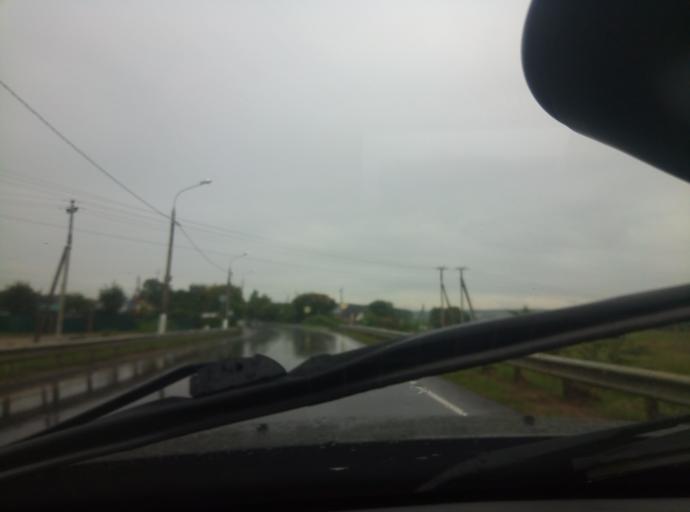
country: RU
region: Kaluga
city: Kremenki
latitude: 54.8807
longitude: 37.1266
